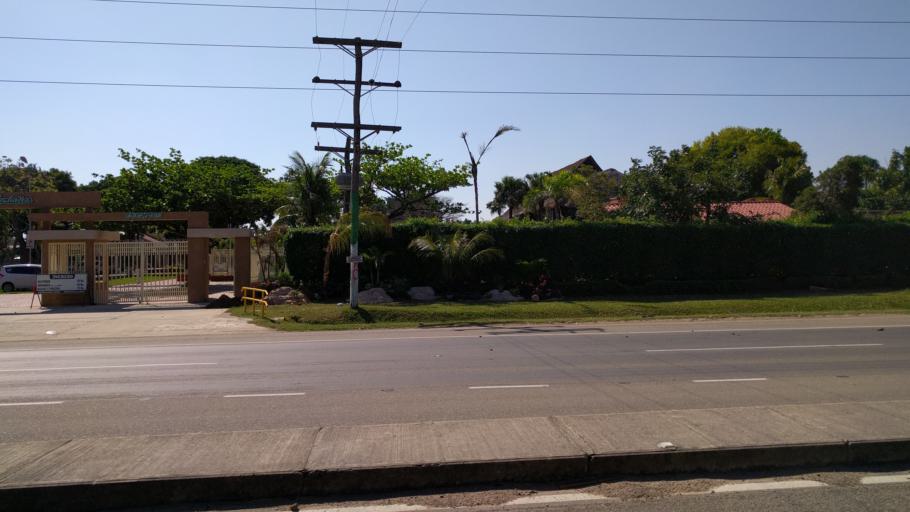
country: BO
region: Santa Cruz
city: Cotoca
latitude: -17.7645
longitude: -63.0349
